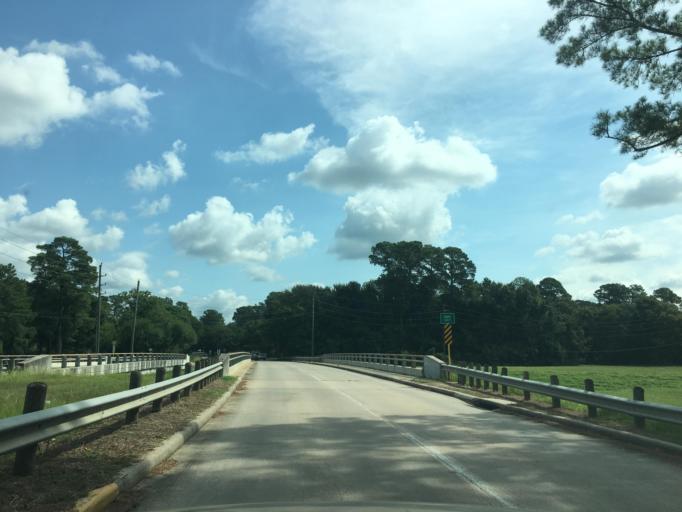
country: US
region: Texas
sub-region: Harris County
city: Spring
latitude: 30.0442
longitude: -95.4470
